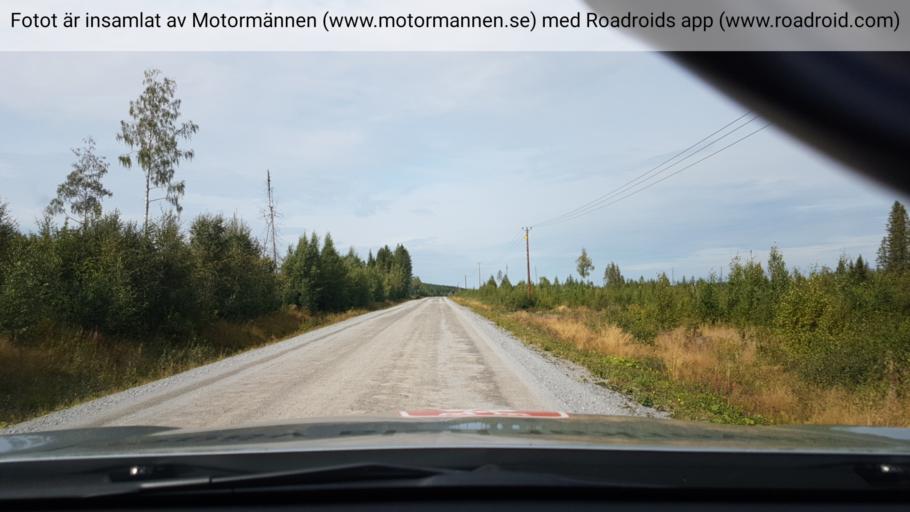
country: SE
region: Vaesterbotten
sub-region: Bjurholms Kommun
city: Bjurholm
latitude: 63.8821
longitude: 19.4360
